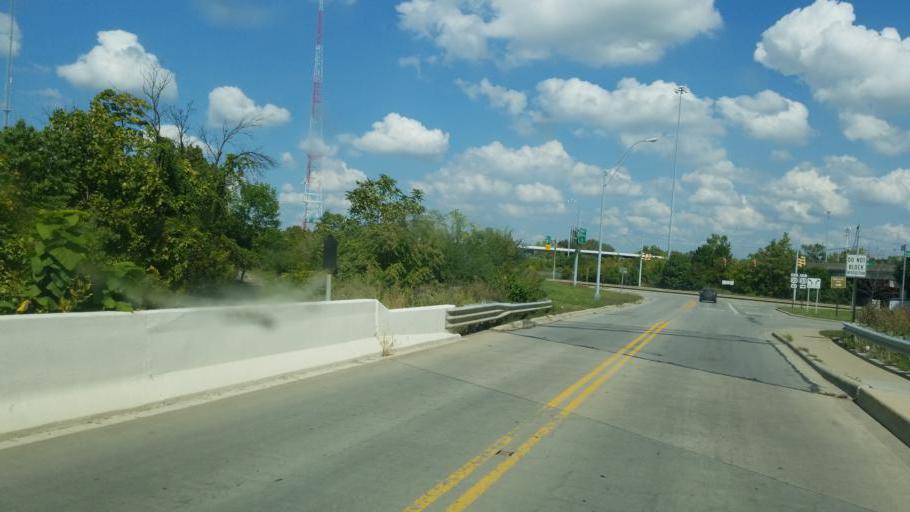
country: US
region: Ohio
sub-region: Franklin County
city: Grandview Heights
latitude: 39.9653
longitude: -83.0224
